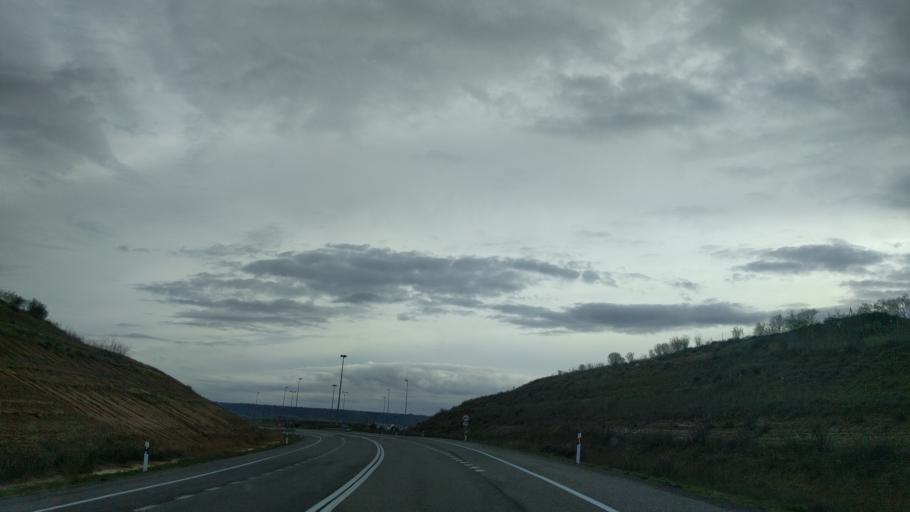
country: ES
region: Aragon
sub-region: Provincia de Huesca
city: Huesca
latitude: 42.1535
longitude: -0.3980
